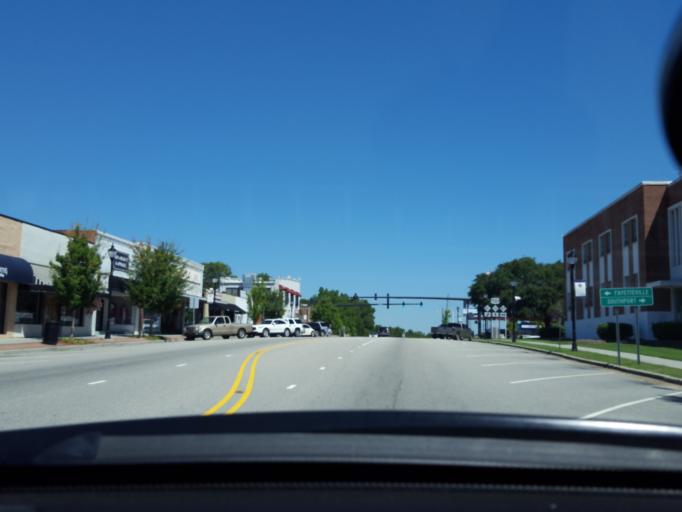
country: US
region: North Carolina
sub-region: Bladen County
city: Elizabethtown
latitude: 34.6278
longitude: -78.6062
